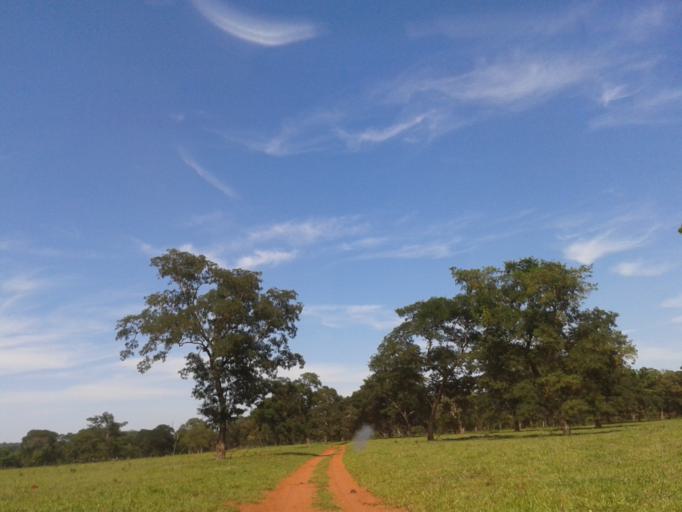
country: BR
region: Minas Gerais
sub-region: Santa Vitoria
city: Santa Vitoria
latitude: -19.1642
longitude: -50.5171
